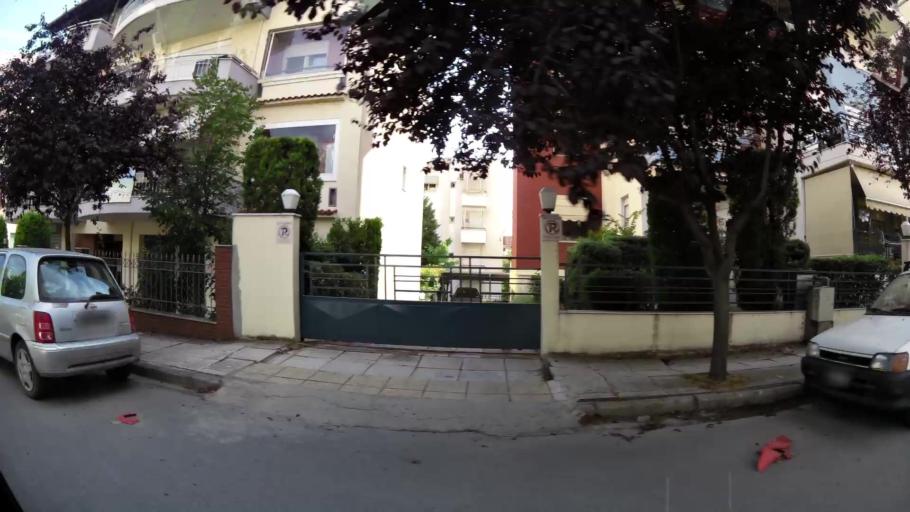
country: GR
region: Central Macedonia
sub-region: Nomos Thessalonikis
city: Kalamaria
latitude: 40.5734
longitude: 22.9655
